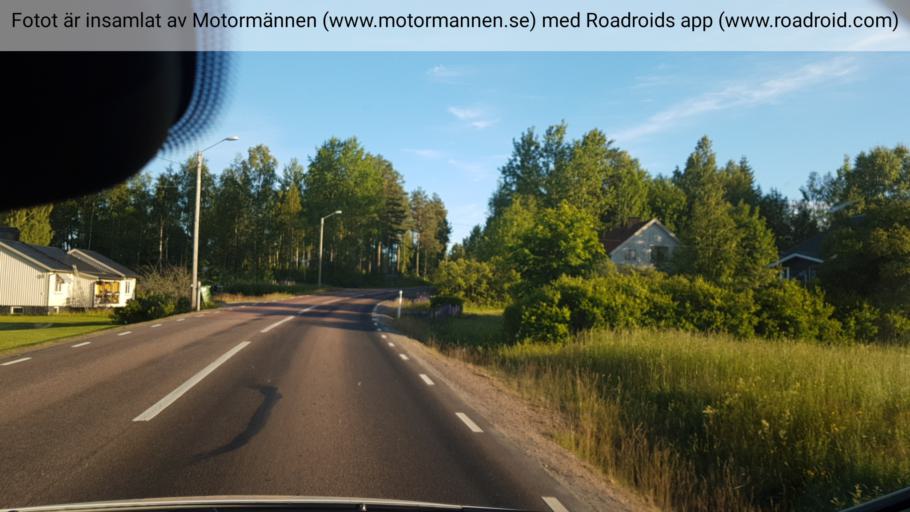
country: SE
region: Vaermland
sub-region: Torsby Kommun
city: Torsby
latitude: 60.2862
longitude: 13.0326
